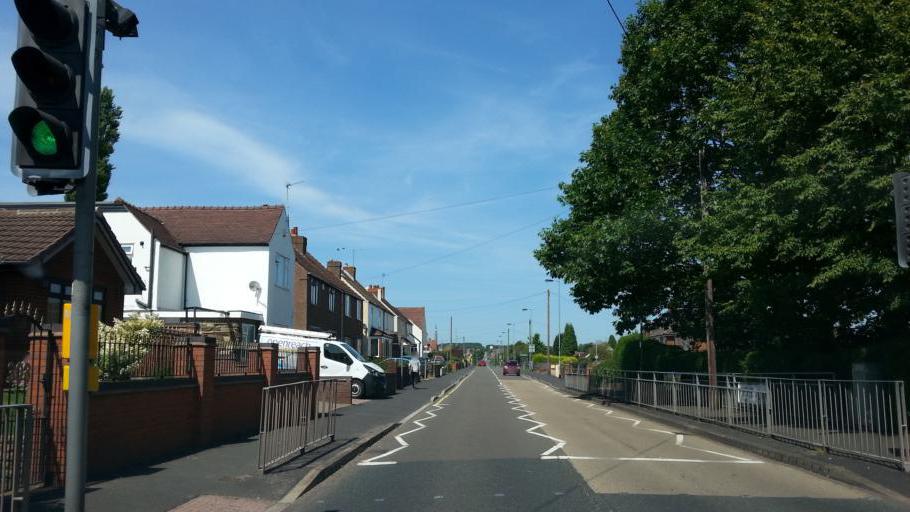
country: GB
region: England
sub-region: Staffordshire
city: Cannock
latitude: 52.7055
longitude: -2.0270
